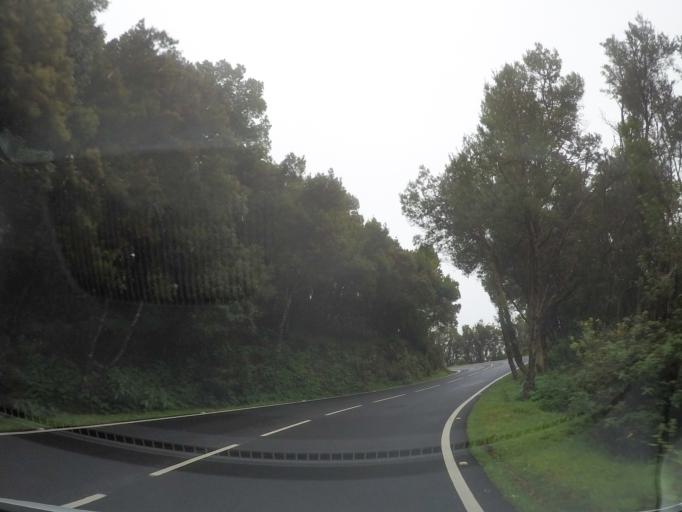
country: ES
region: Canary Islands
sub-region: Provincia de Santa Cruz de Tenerife
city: Vallehermosa
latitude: 28.1266
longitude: -17.2626
